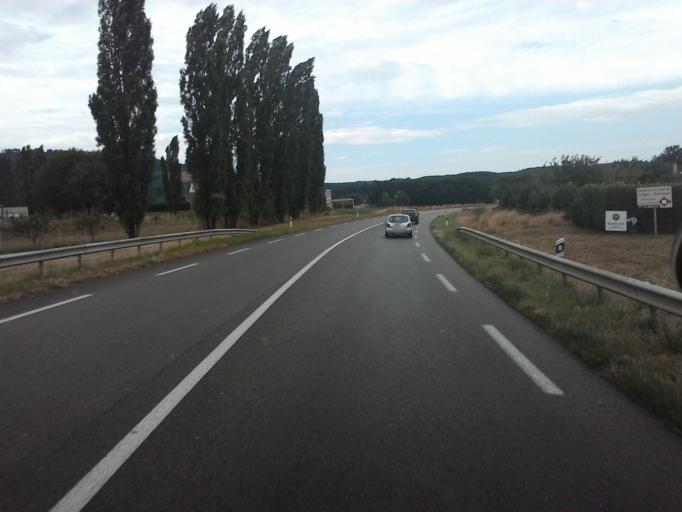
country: FR
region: Franche-Comte
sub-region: Departement du Jura
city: Poligny
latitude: 46.8386
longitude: 5.6976
